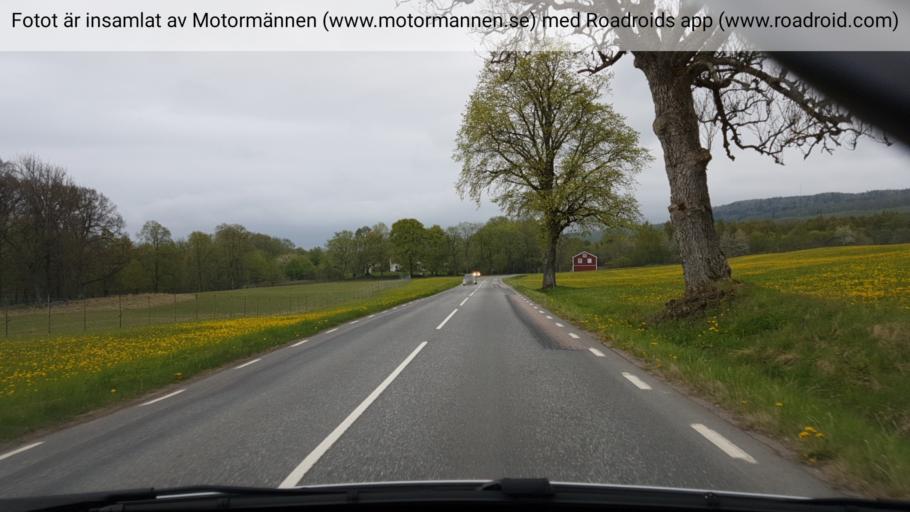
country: SE
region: Vaestra Goetaland
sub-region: Skovde Kommun
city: Stopen
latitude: 58.4574
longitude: 13.8401
